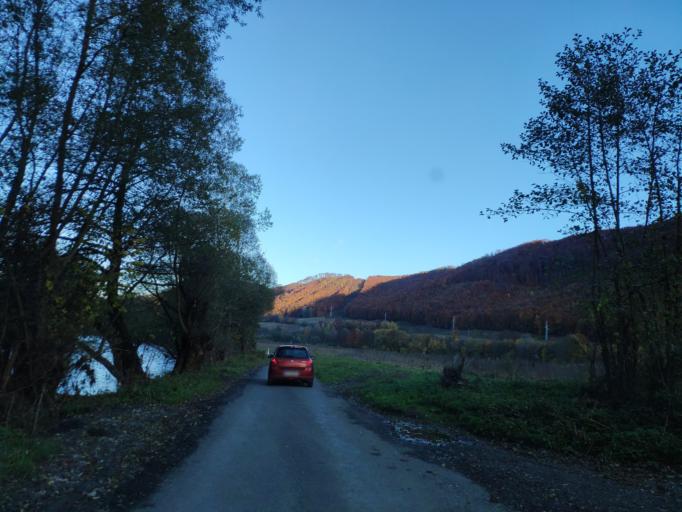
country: SK
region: Presovsky
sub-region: Okres Presov
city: Presov
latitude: 48.8535
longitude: 21.1739
